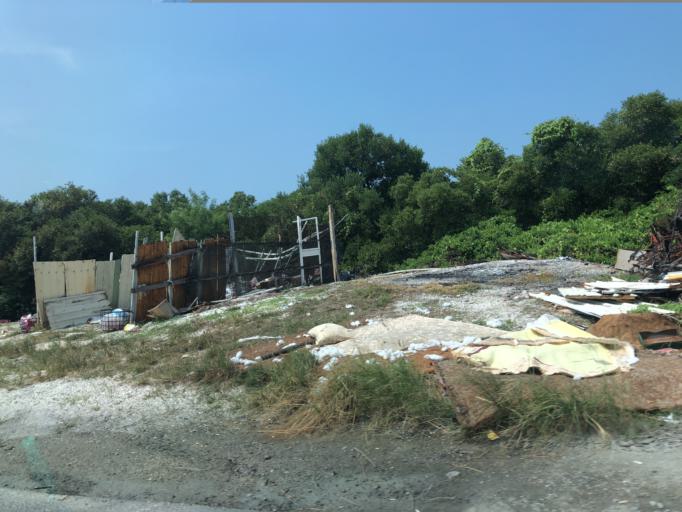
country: TW
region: Taiwan
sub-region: Chiayi
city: Taibao
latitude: 23.4593
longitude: 120.1509
